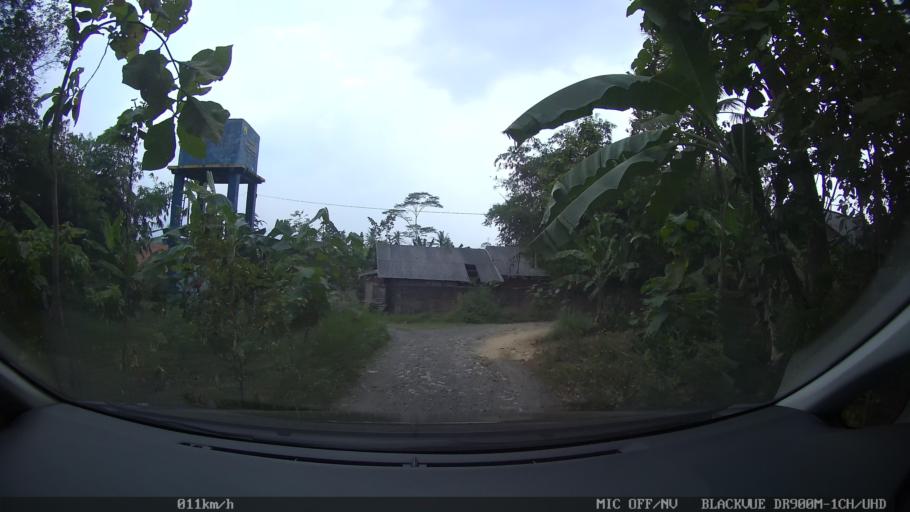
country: ID
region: Lampung
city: Gadingrejo
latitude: -5.3917
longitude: 105.0368
